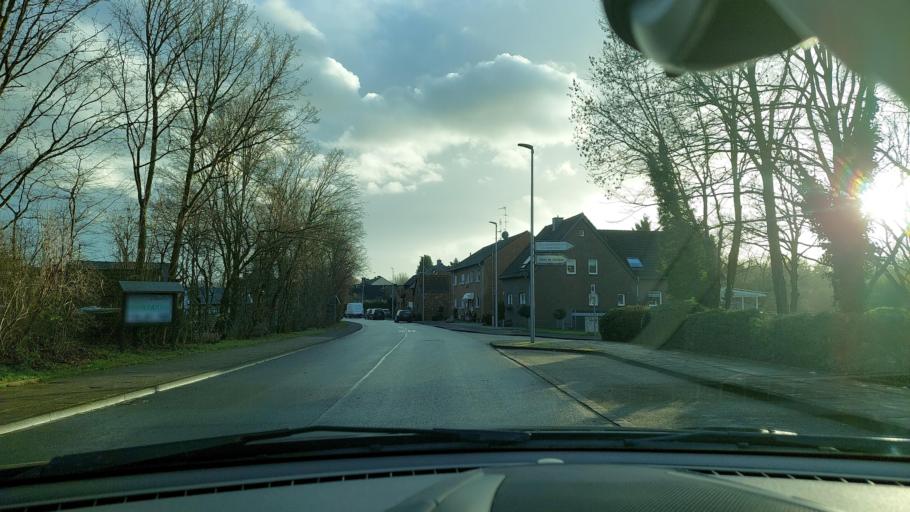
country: DE
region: North Rhine-Westphalia
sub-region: Regierungsbezirk Koln
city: Sinnersdorf
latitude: 51.0582
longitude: 6.8168
